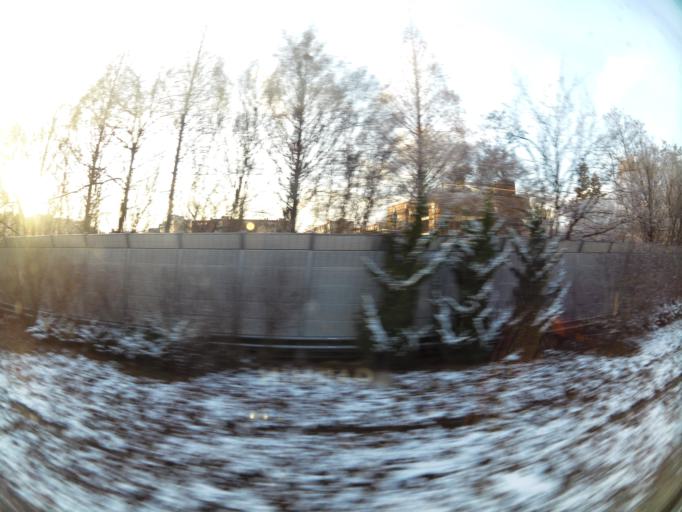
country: KR
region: Daejeon
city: Daejeon
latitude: 36.3666
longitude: 127.4199
